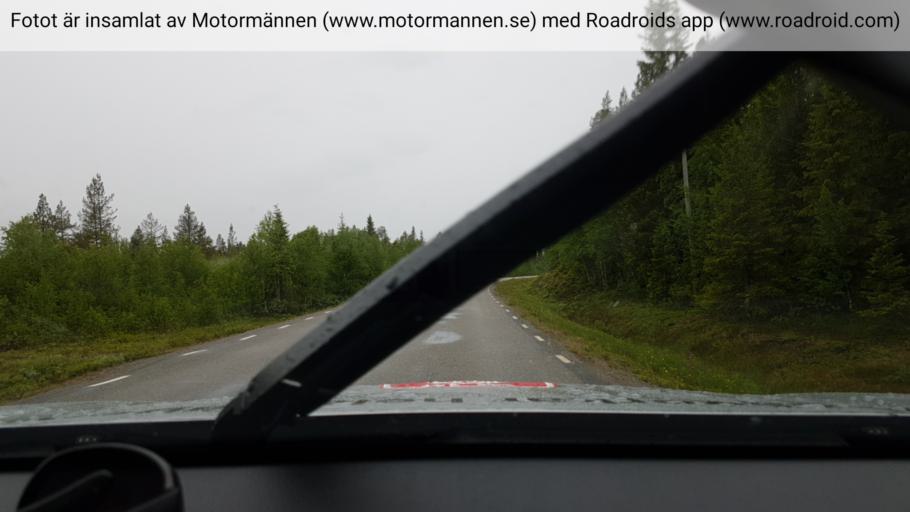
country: SE
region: Vaesterbotten
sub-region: Storumans Kommun
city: Fristad
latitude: 65.8528
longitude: 16.5441
